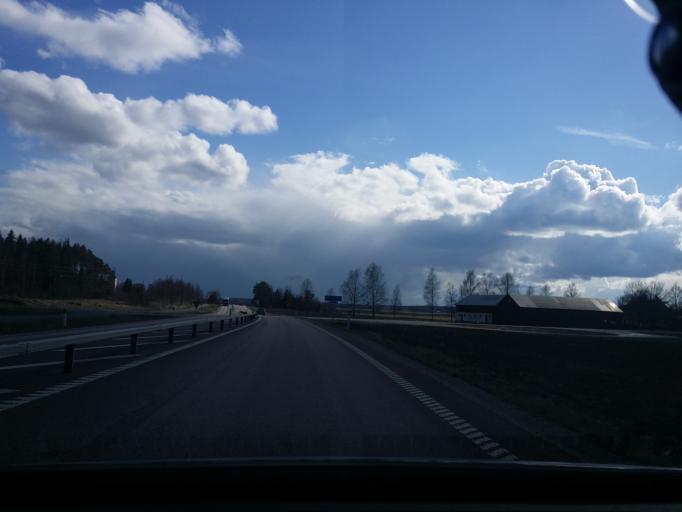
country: SE
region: Vaestmanland
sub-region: Sala Kommun
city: Sala
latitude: 59.8778
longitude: 16.5448
